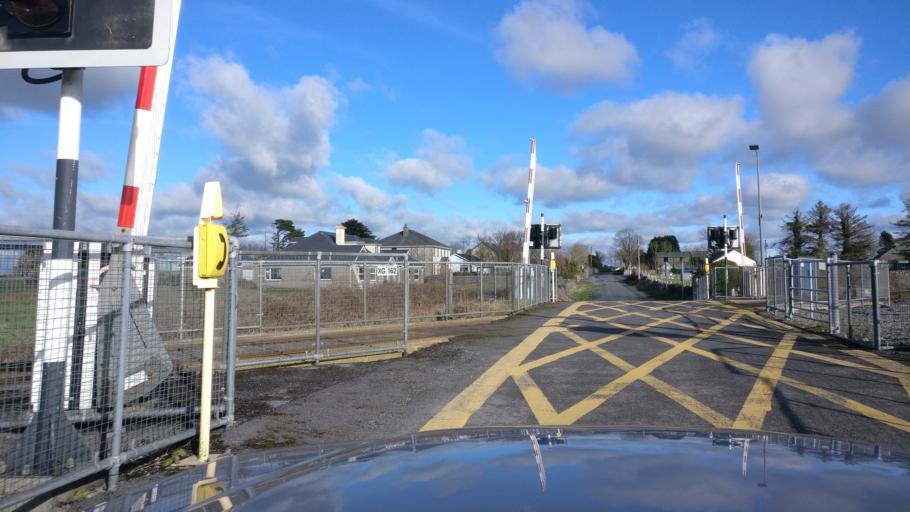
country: IE
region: Connaught
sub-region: County Galway
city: Oranmore
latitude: 53.2811
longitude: -8.9005
